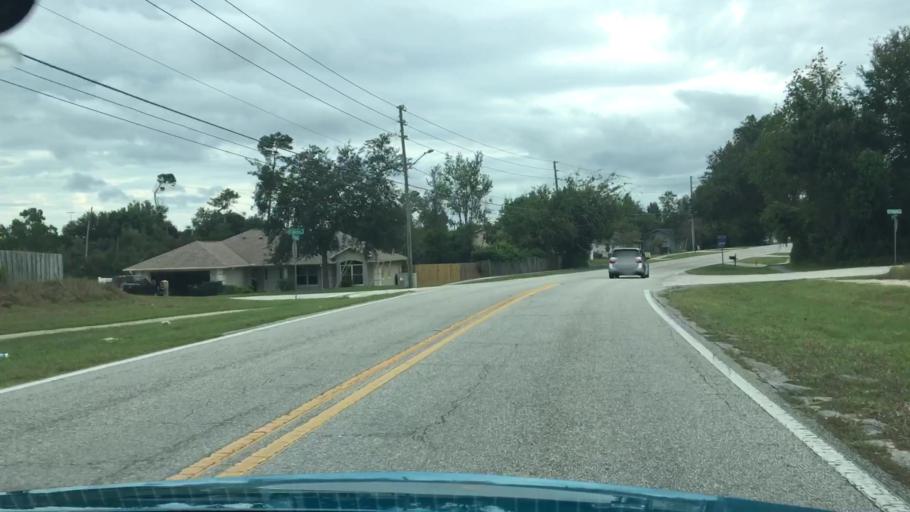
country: US
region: Florida
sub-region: Volusia County
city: Deltona
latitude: 28.9116
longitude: -81.2212
